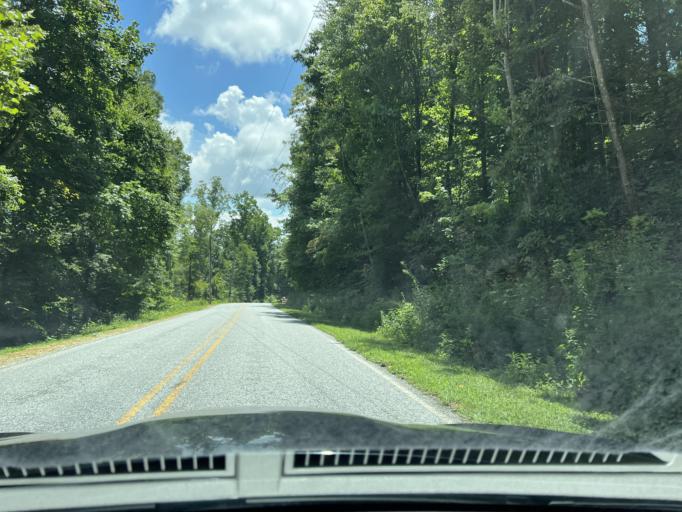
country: US
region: North Carolina
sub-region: Henderson County
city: Fruitland
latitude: 35.4167
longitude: -82.4019
